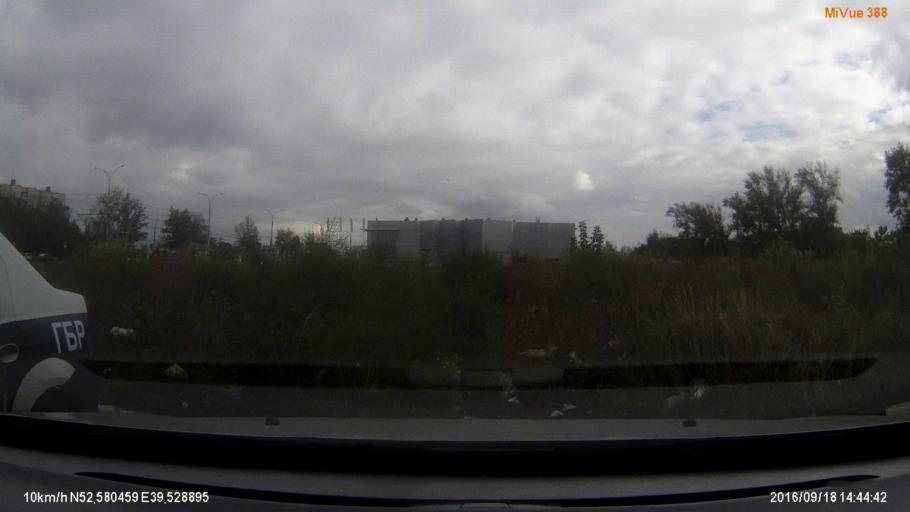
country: RU
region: Lipetsk
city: Syrskoye
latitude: 52.5806
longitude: 39.5292
